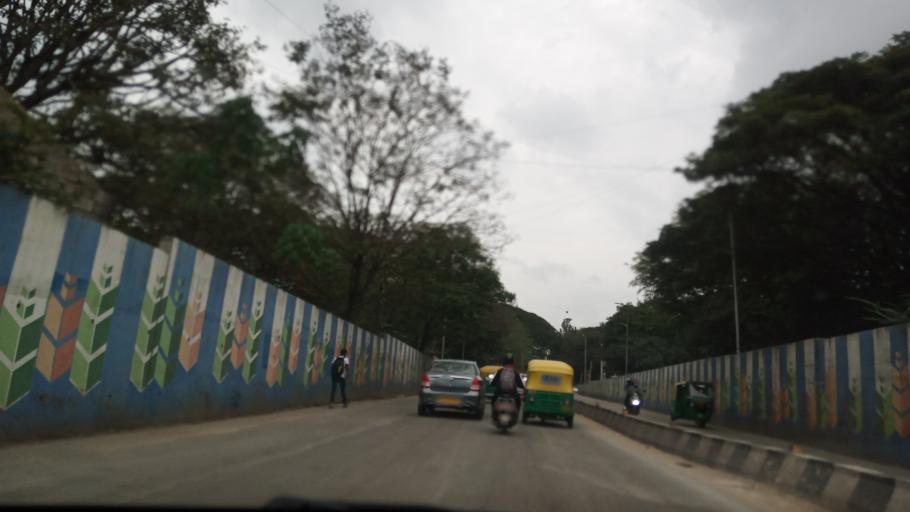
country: IN
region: Karnataka
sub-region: Bangalore Urban
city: Bangalore
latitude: 12.9949
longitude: 77.5961
